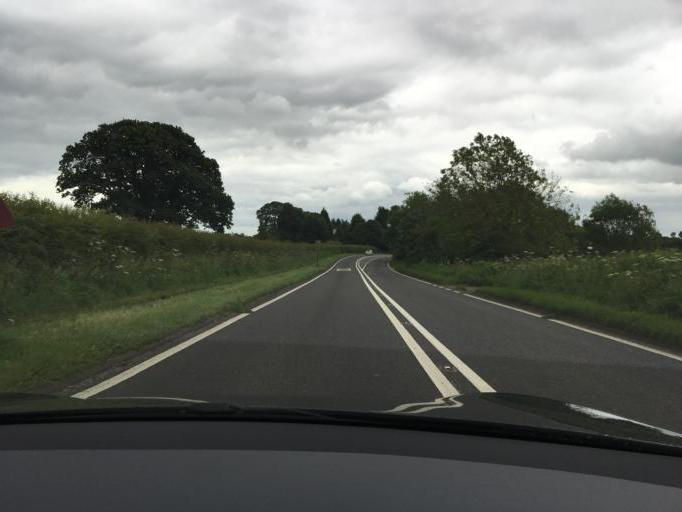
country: GB
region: England
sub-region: Derbyshire
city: Shirley
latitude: 52.9914
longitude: -1.6888
